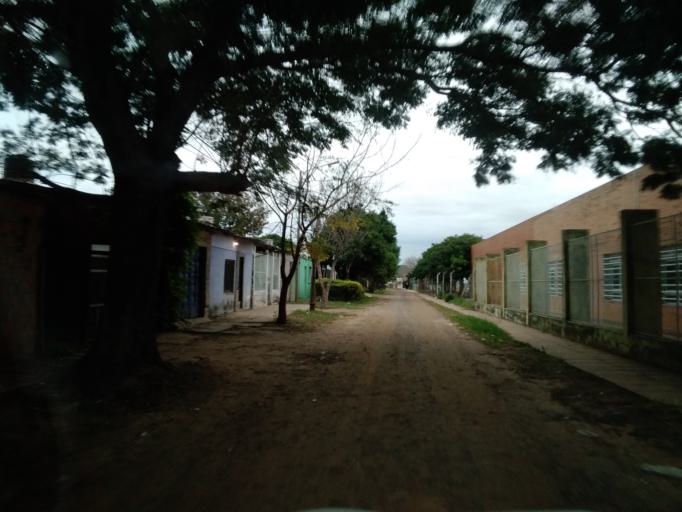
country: AR
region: Corrientes
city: Corrientes
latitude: -27.5084
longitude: -58.7925
